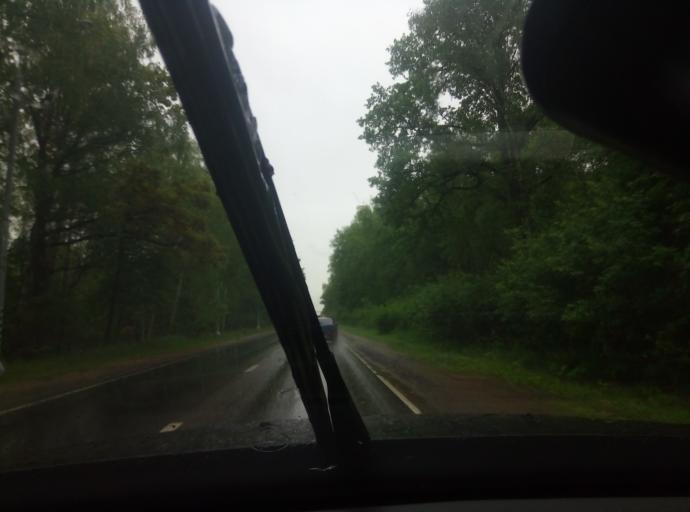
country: RU
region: Moskovskaya
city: Protvino
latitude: 54.8857
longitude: 37.1891
